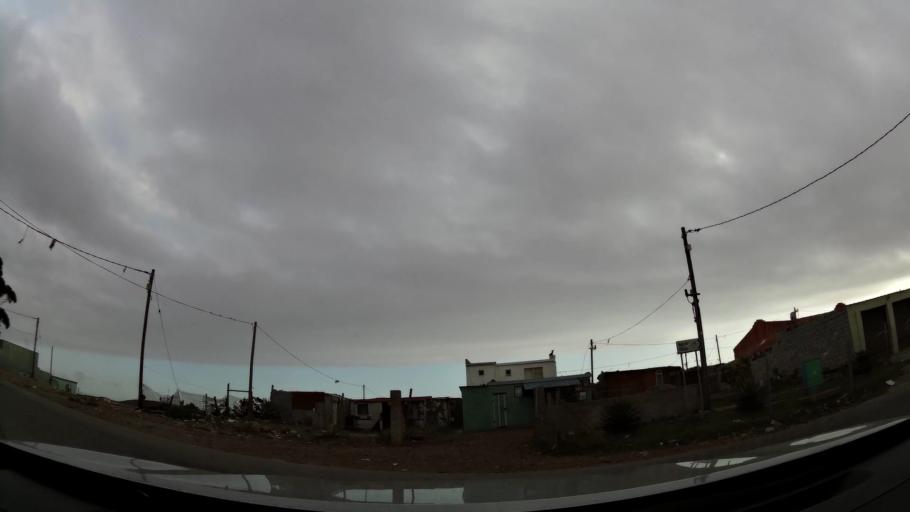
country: ZA
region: Eastern Cape
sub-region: Nelson Mandela Bay Metropolitan Municipality
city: Port Elizabeth
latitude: -33.9108
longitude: 25.5382
